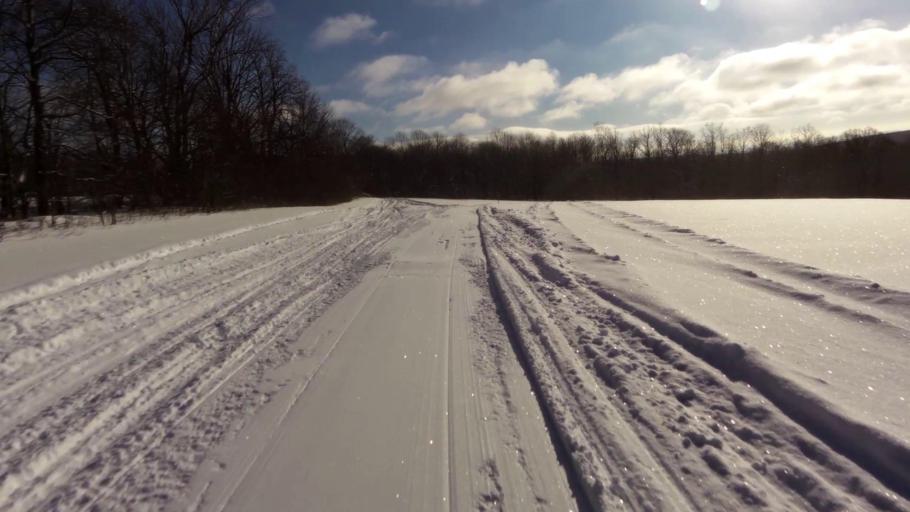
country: US
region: New York
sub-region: Chautauqua County
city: Falconer
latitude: 42.2606
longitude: -79.1750
